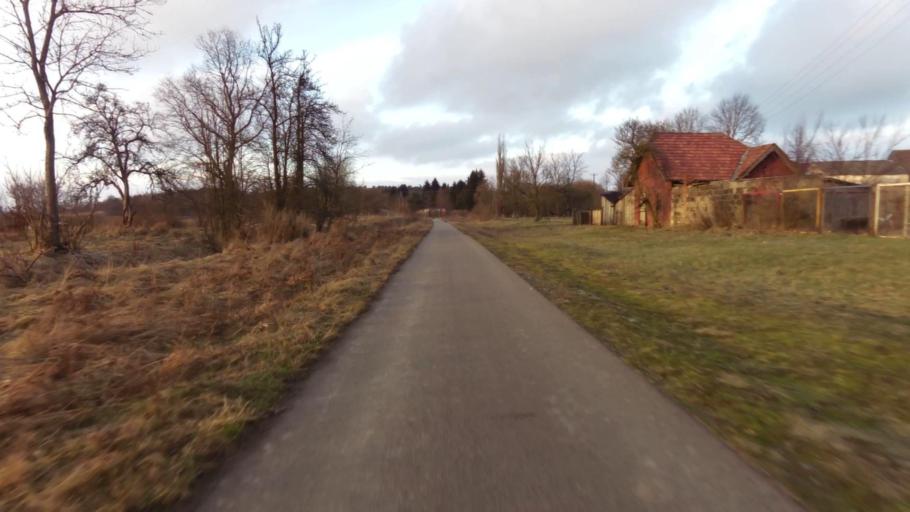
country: PL
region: West Pomeranian Voivodeship
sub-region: Powiat drawski
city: Zlocieniec
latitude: 53.6310
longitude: 16.0560
